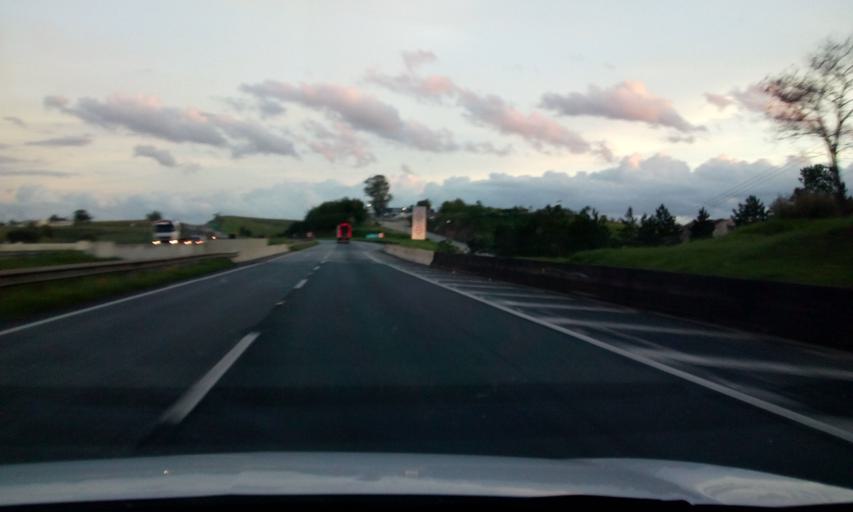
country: BR
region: Sao Paulo
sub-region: Jacarei
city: Jacarei
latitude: -23.2703
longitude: -46.0587
